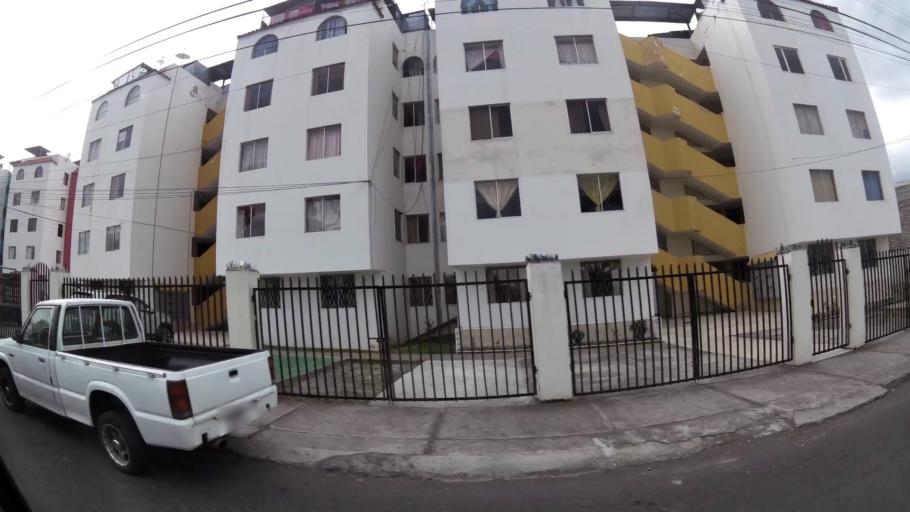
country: EC
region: Tungurahua
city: Ambato
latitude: -1.2743
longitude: -78.6252
